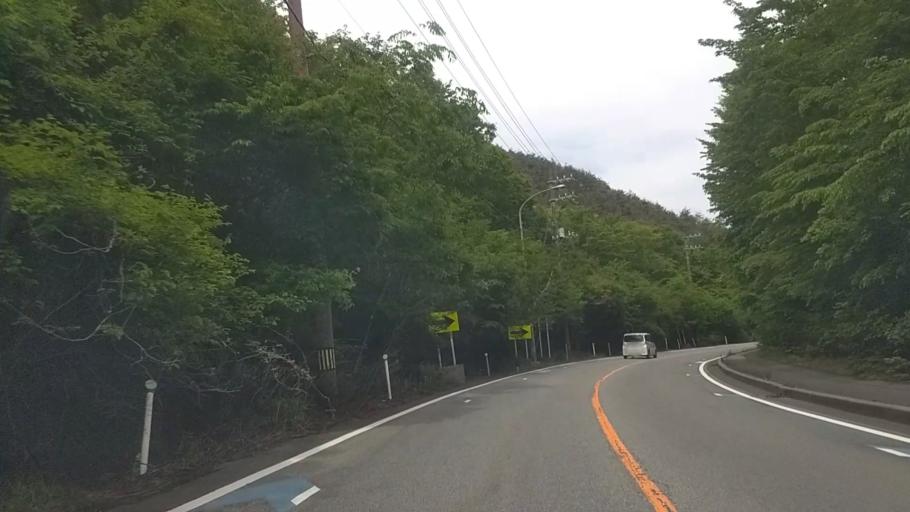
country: JP
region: Yamanashi
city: Fujikawaguchiko
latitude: 35.4864
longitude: 138.6346
